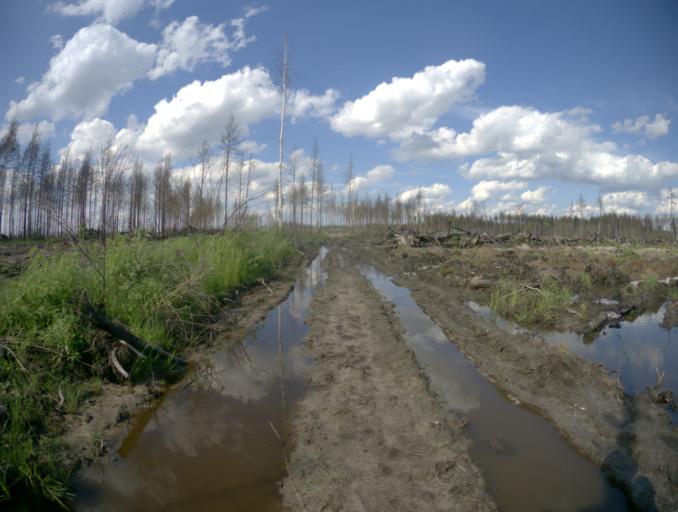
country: RU
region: Vladimir
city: Velikodvorskiy
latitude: 55.3124
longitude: 40.9183
